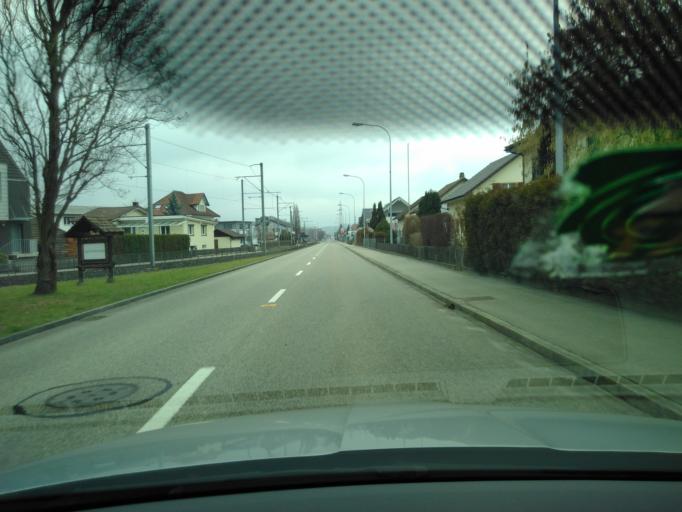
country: CH
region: Aargau
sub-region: Bezirk Aarau
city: Muhen
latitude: 47.3417
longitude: 8.0539
